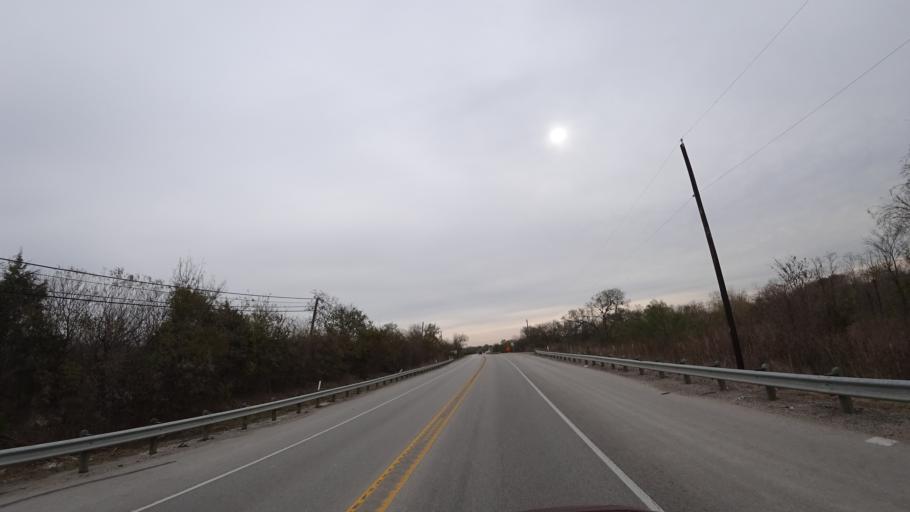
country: US
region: Texas
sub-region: Travis County
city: Garfield
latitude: 30.1183
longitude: -97.6326
